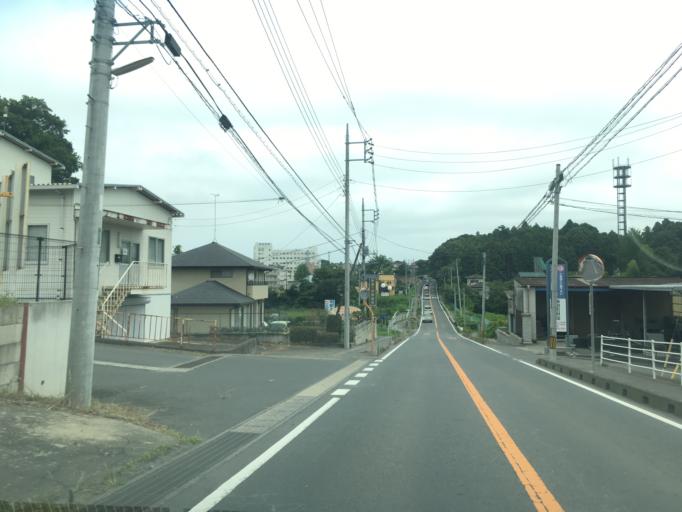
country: JP
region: Ibaraki
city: Katsuta
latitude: 36.3827
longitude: 140.5400
